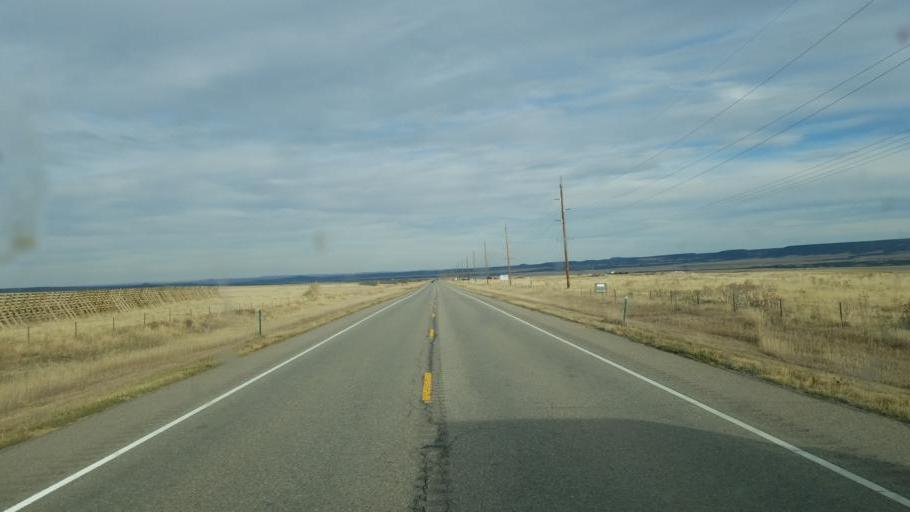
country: US
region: Colorado
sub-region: Huerfano County
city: Walsenburg
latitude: 37.5421
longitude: -105.0472
